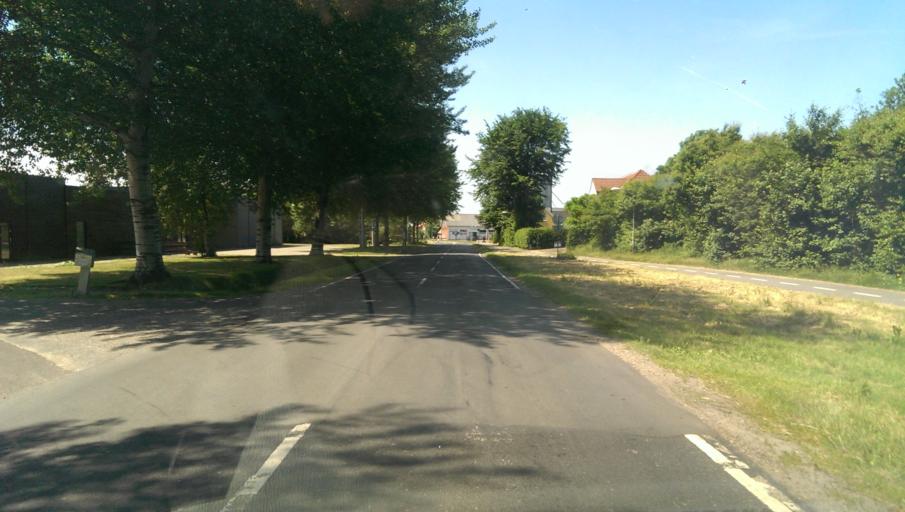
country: DK
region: South Denmark
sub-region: Esbjerg Kommune
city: Esbjerg
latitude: 55.5309
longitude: 8.4057
